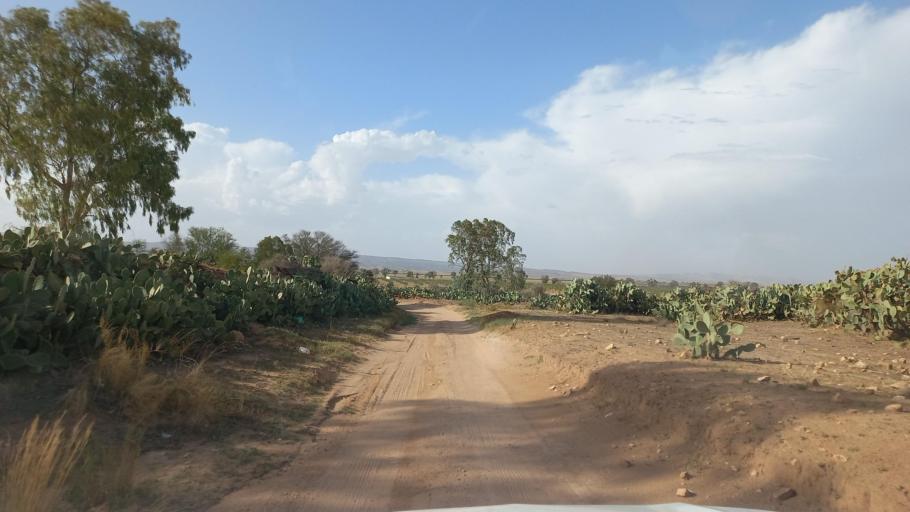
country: TN
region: Al Qasrayn
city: Kasserine
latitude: 35.2254
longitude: 8.9693
